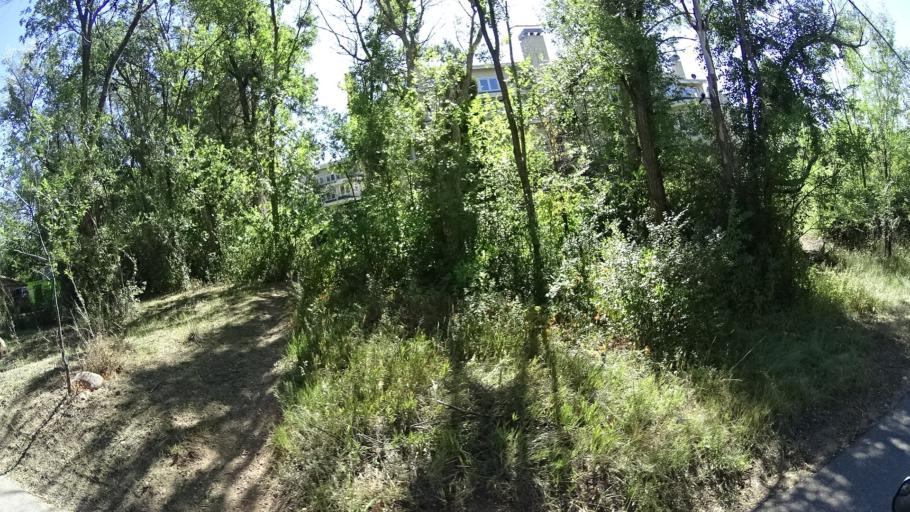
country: US
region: Colorado
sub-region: El Paso County
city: Colorado Springs
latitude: 38.8425
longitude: -104.8429
